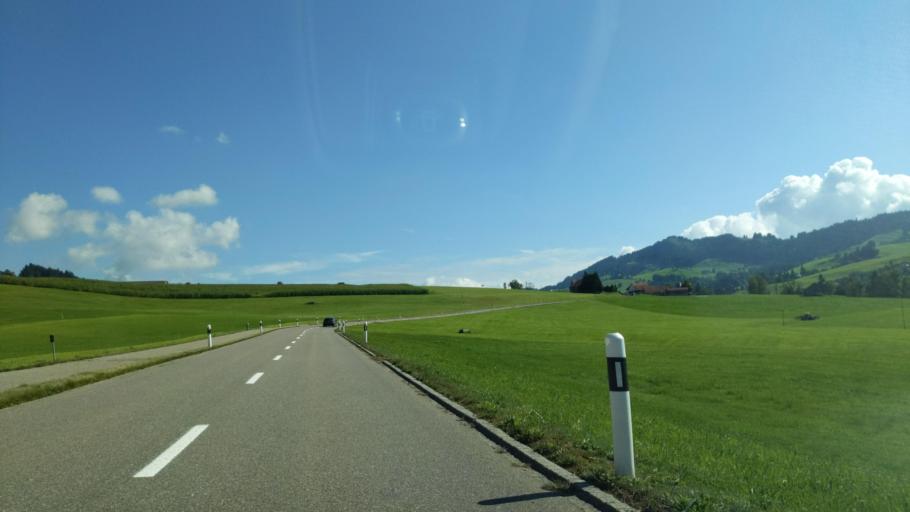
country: CH
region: Saint Gallen
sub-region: Wahlkreis Toggenburg
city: Sankt Peterzell
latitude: 47.3199
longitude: 9.1943
